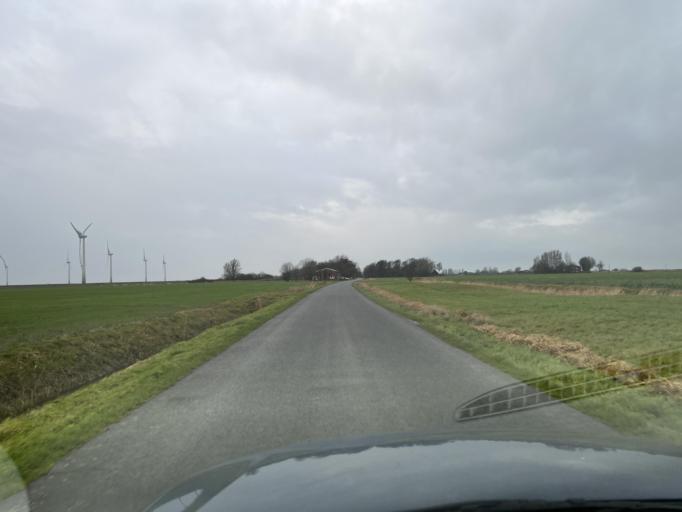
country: DE
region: Schleswig-Holstein
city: Hillgroven
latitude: 54.2161
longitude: 8.8822
